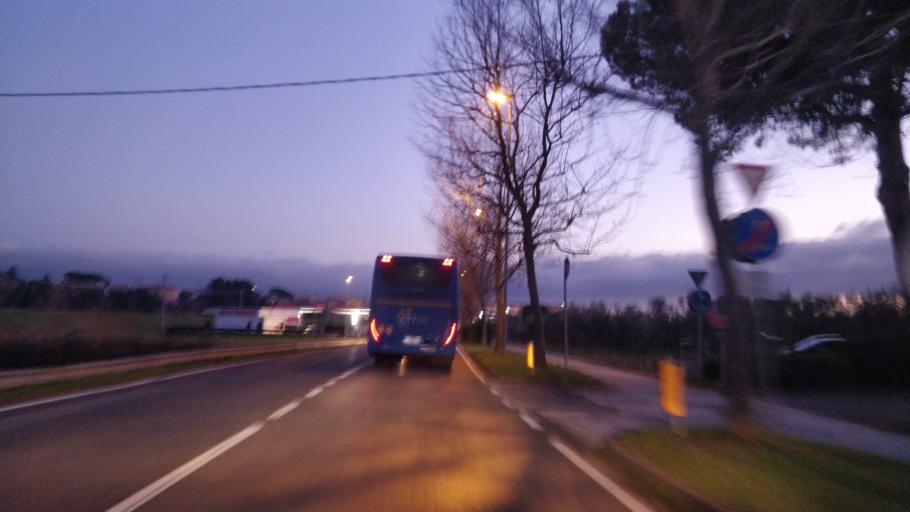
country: IT
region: Tuscany
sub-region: Provincia di Livorno
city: S.P. in Palazzi
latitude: 43.3187
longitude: 10.5127
